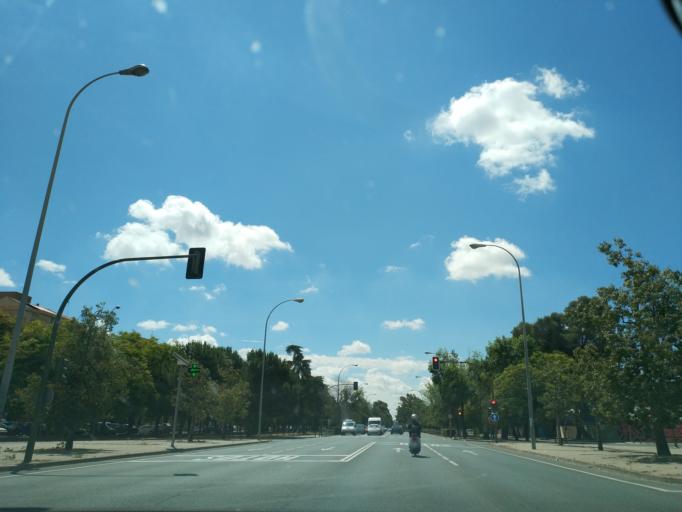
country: ES
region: Andalusia
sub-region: Provincia de Sevilla
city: Sevilla
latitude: 37.3672
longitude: -5.9665
